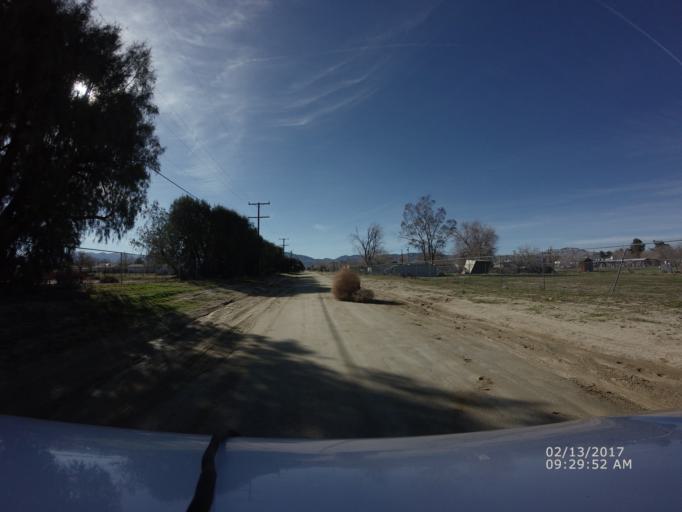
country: US
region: California
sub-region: Los Angeles County
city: Littlerock
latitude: 34.5406
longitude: -117.9625
